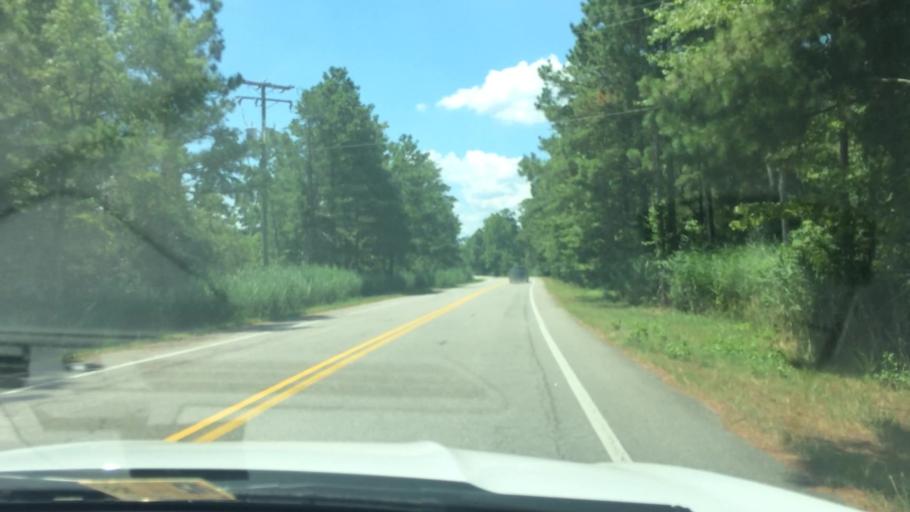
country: US
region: Virginia
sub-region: King William County
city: West Point
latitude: 37.5452
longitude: -76.7932
